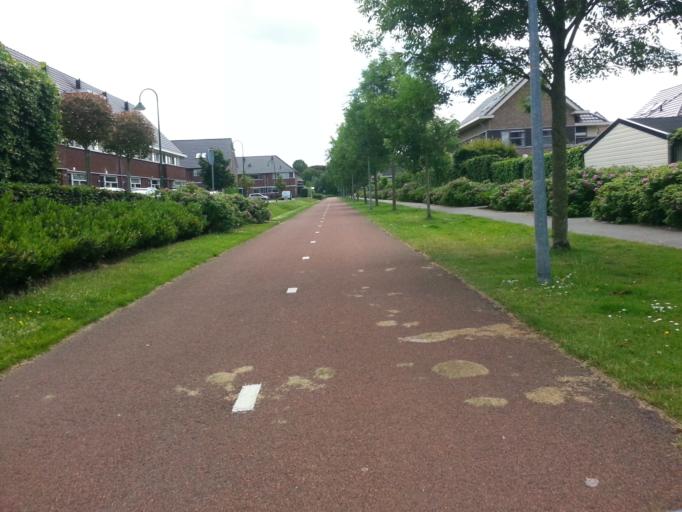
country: NL
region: Gelderland
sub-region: Gemeente Barneveld
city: Barneveld
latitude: 52.1288
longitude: 5.5739
